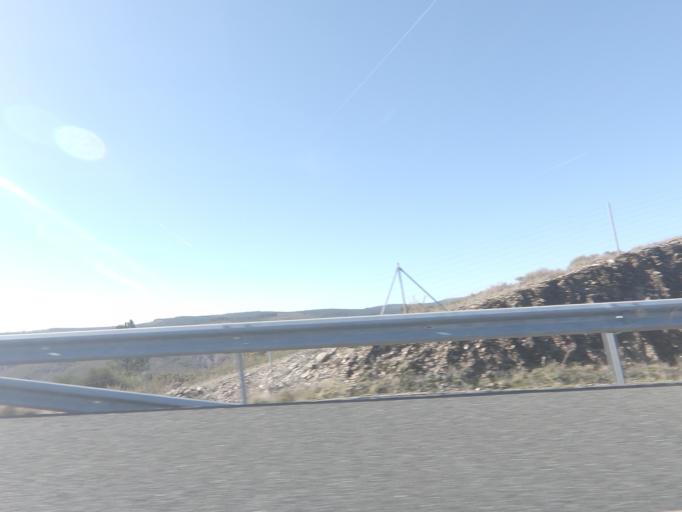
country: ES
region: Galicia
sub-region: Provincia de Pontevedra
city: Dozon
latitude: 42.5812
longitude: -8.0686
